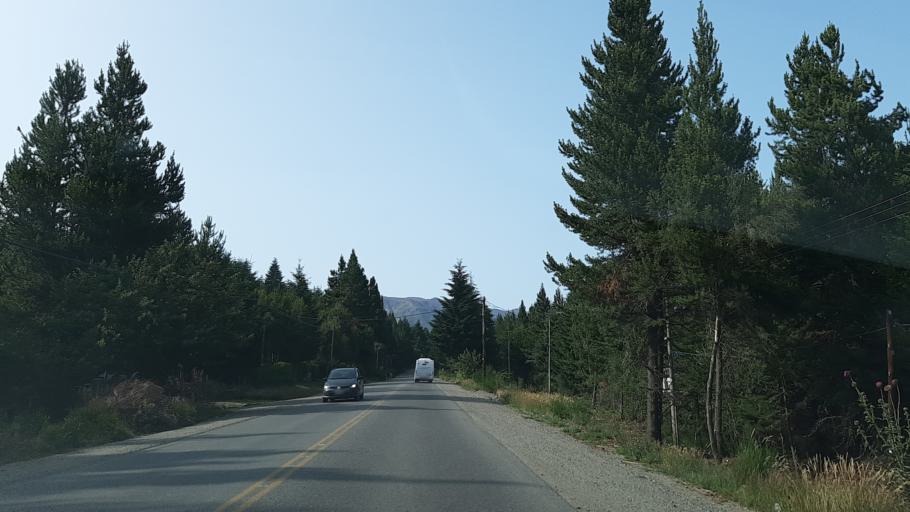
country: AR
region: Rio Negro
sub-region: Departamento de Bariloche
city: San Carlos de Bariloche
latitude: -41.1536
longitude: -71.4085
